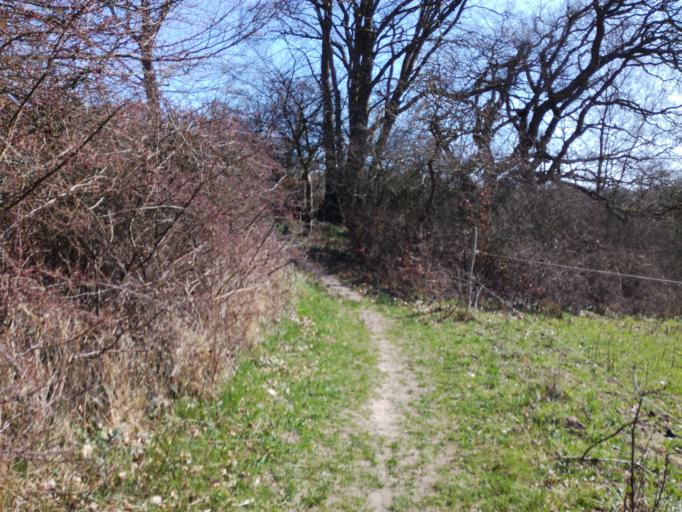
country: DK
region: South Denmark
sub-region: Fredericia Kommune
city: Fredericia
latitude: 55.6246
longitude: 9.8426
